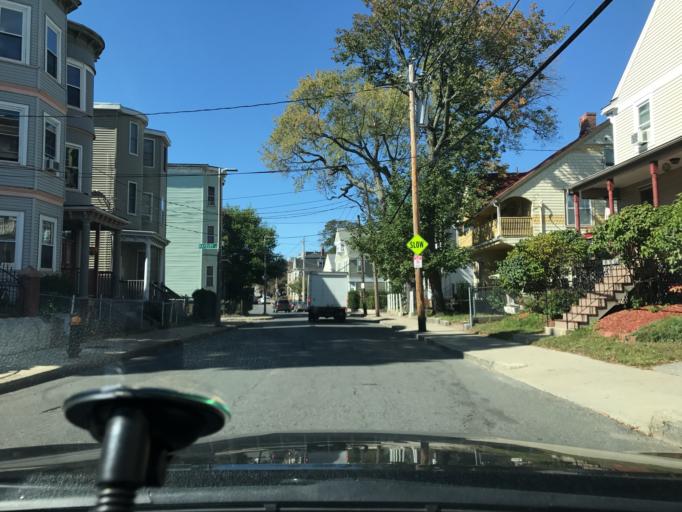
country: US
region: Massachusetts
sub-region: Suffolk County
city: South Boston
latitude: 42.3155
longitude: -71.0806
